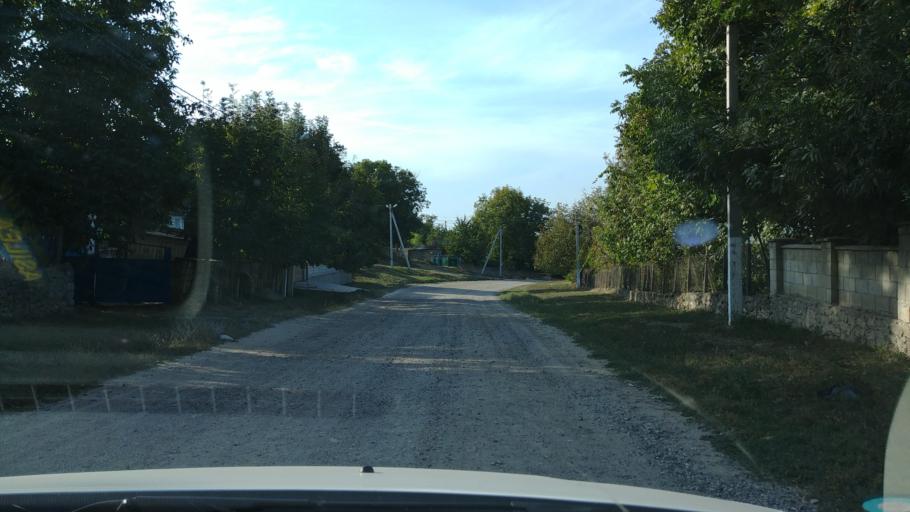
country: MD
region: Rezina
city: Rezina
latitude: 47.7471
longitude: 28.8858
